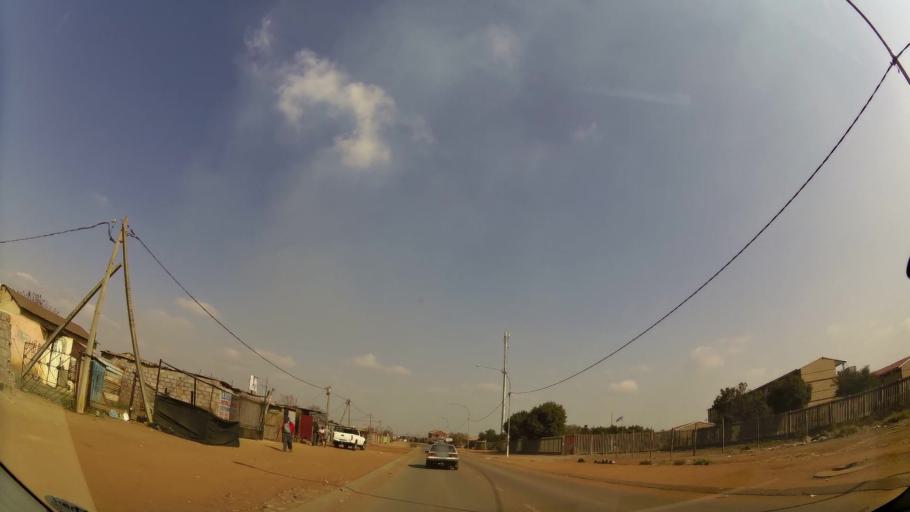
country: ZA
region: Gauteng
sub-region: Ekurhuleni Metropolitan Municipality
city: Springs
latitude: -26.1079
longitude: 28.4810
